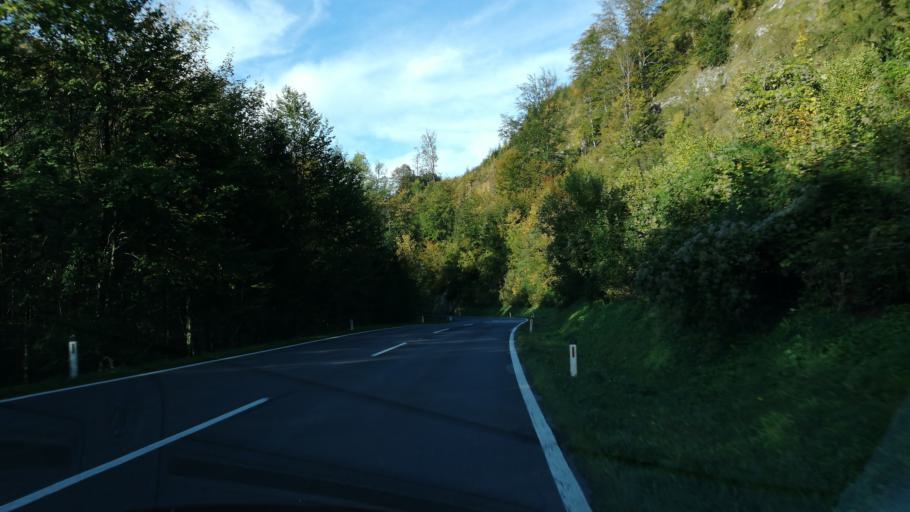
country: AT
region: Styria
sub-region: Politischer Bezirk Liezen
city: Altenmarkt bei Sankt Gallen
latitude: 47.7606
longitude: 14.6469
